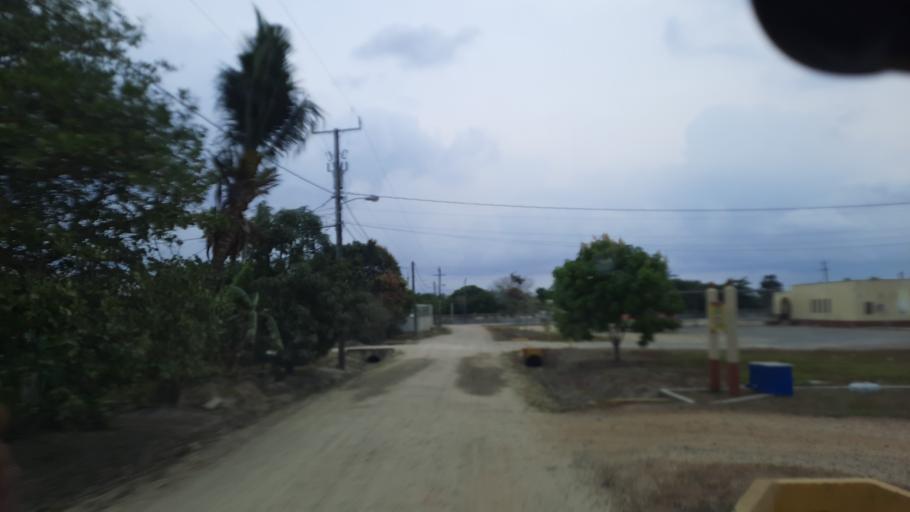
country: BZ
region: Stann Creek
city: Placencia
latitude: 16.5342
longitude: -88.4241
